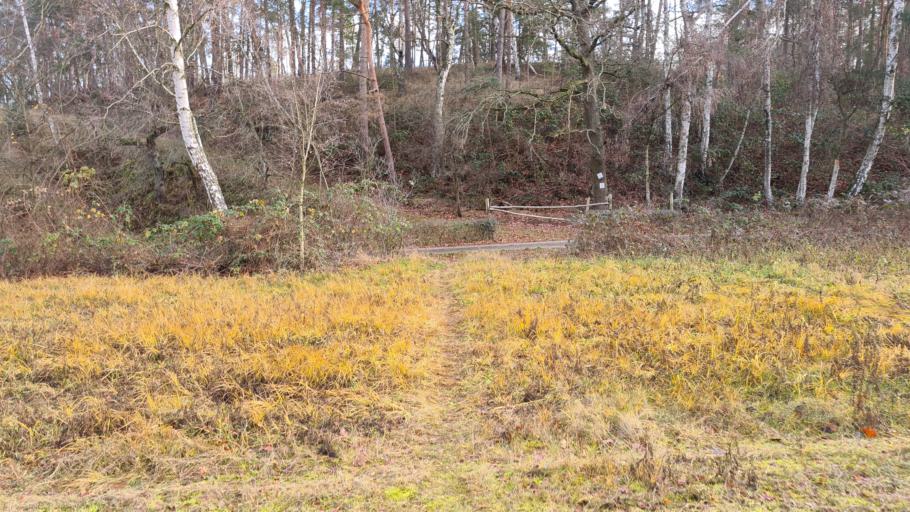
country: DE
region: Brandenburg
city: Groden
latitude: 51.3911
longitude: 13.5843
